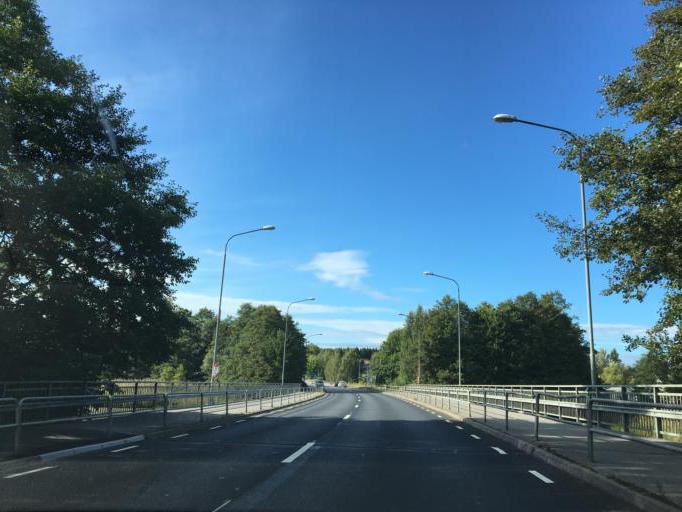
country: SE
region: Soedermanland
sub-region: Nykopings Kommun
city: Nykoping
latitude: 58.7750
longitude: 16.9809
